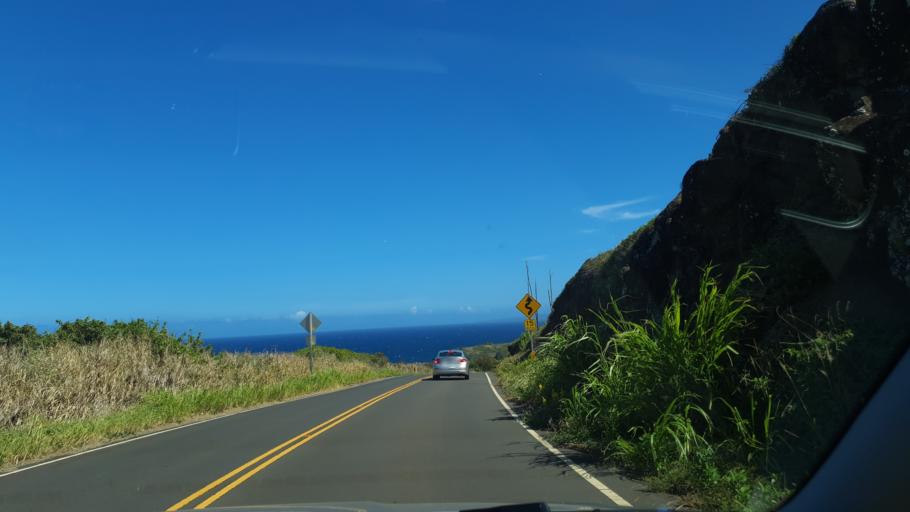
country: US
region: Hawaii
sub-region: Maui County
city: Napili-Honokowai
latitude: 21.0142
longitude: -156.5718
